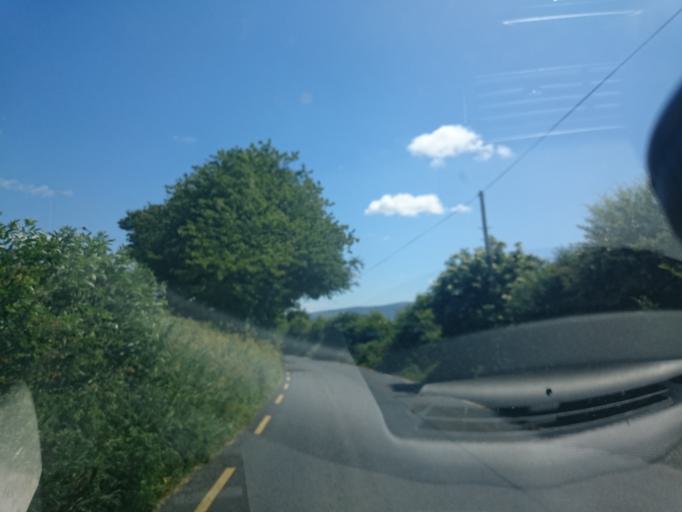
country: IE
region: Leinster
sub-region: Kilkenny
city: Graiguenamanagh
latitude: 52.5921
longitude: -6.9818
